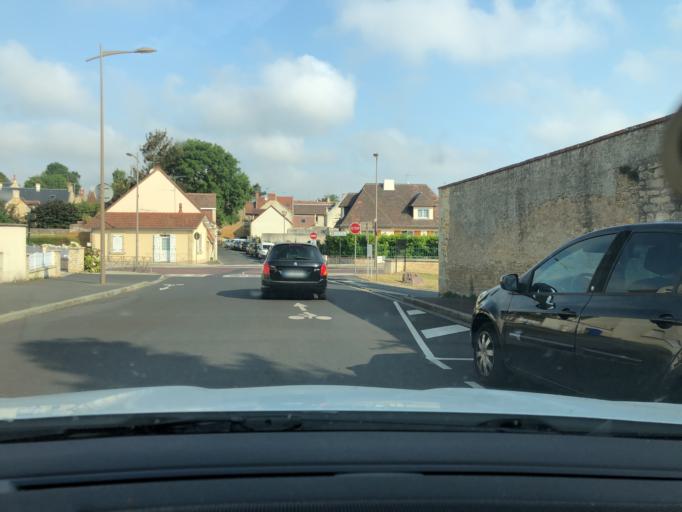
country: FR
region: Lower Normandy
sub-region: Departement du Calvados
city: Douvres-la-Delivrande
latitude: 49.2963
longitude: -0.3739
